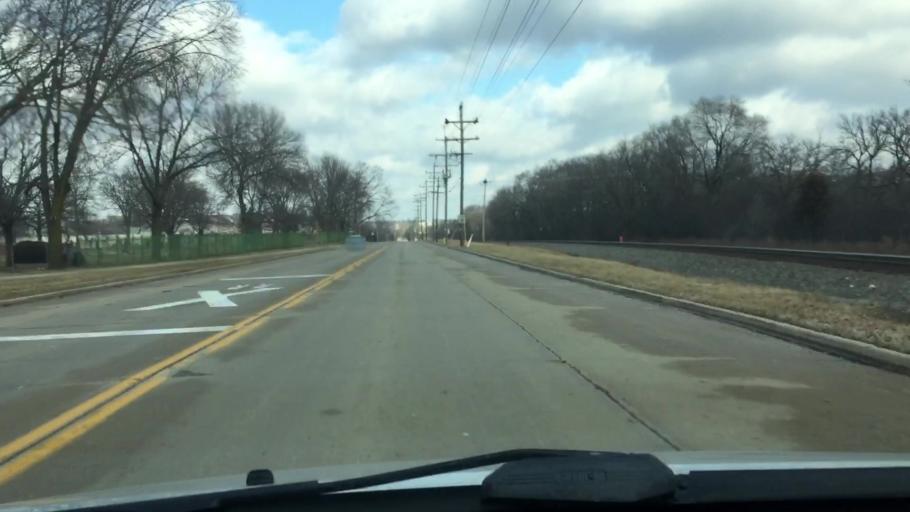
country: US
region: Wisconsin
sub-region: Waukesha County
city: Waukesha
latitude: 42.9944
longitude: -88.2370
